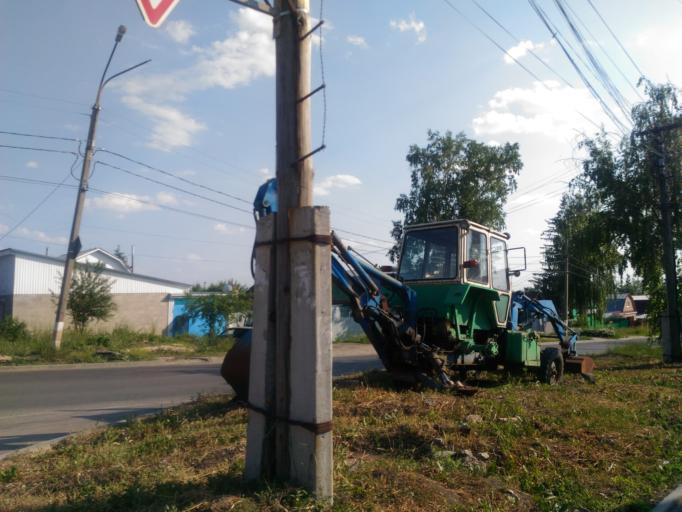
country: RU
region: Ulyanovsk
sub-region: Ulyanovskiy Rayon
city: Ulyanovsk
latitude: 54.3390
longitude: 48.3628
